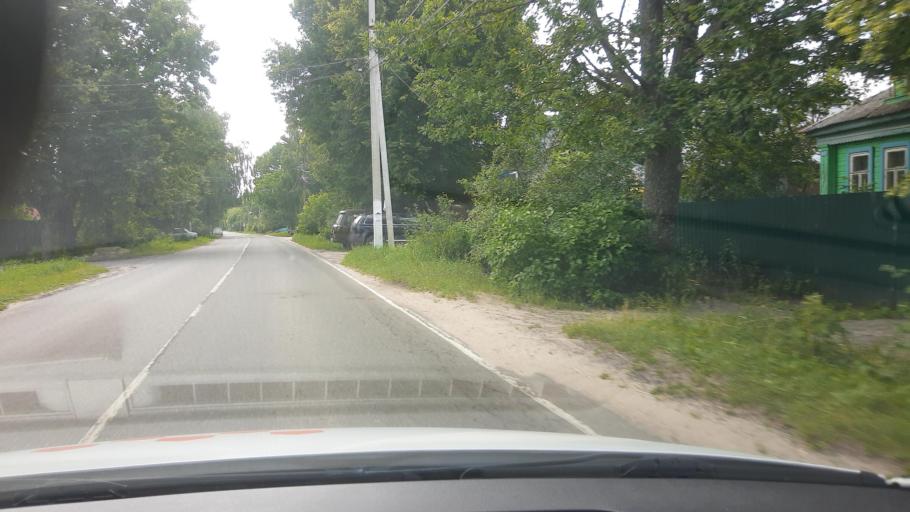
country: RU
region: Moskovskaya
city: Fryazevo
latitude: 55.7240
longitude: 38.4368
